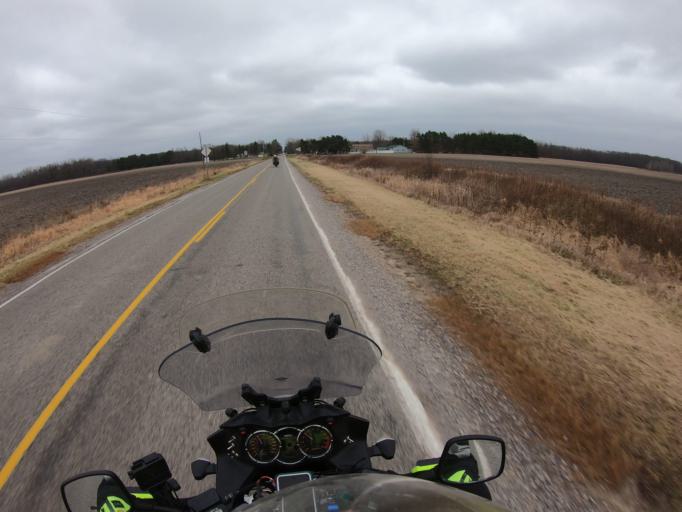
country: US
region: Michigan
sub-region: Saginaw County
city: Burt
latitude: 43.2492
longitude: -83.9823
